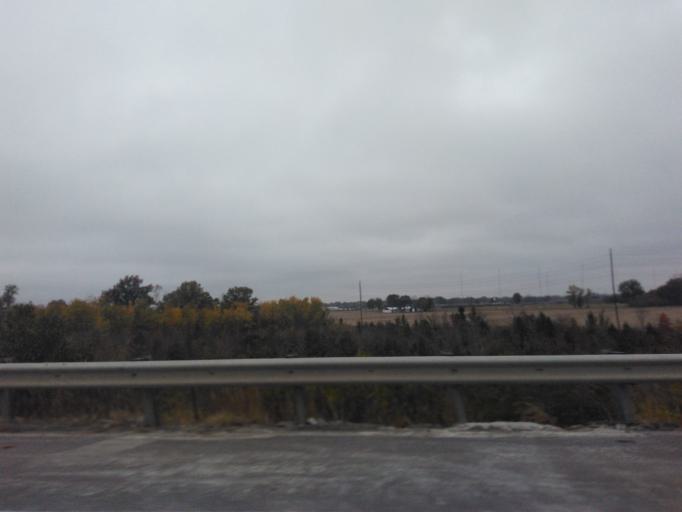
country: US
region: Illinois
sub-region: Saint Clair County
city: Washington Park
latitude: 38.6105
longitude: -90.0794
